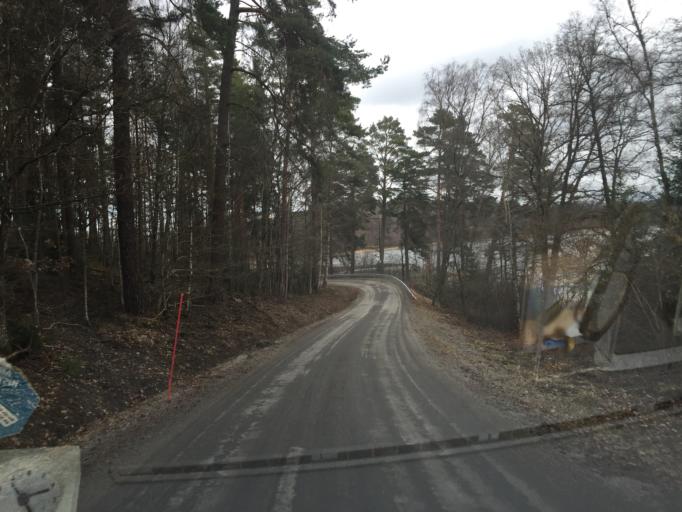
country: SE
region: Stockholm
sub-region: Salems Kommun
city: Ronninge
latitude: 59.2571
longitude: 17.6987
